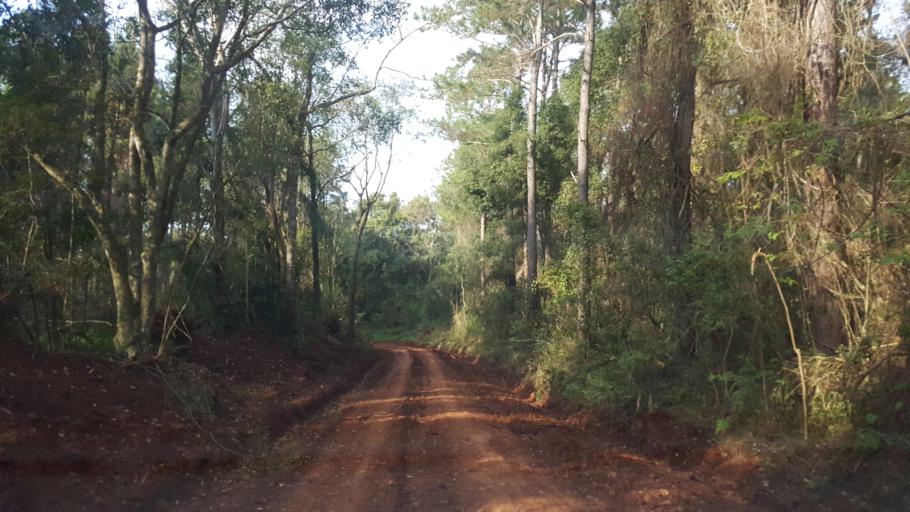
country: AR
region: Misiones
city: Capiovi
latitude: -26.9001
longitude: -55.1071
